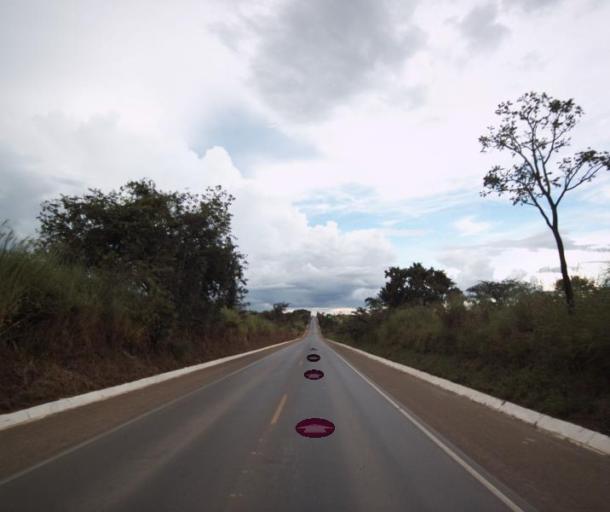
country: BR
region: Goias
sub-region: Itapaci
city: Itapaci
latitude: -14.8863
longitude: -49.3402
